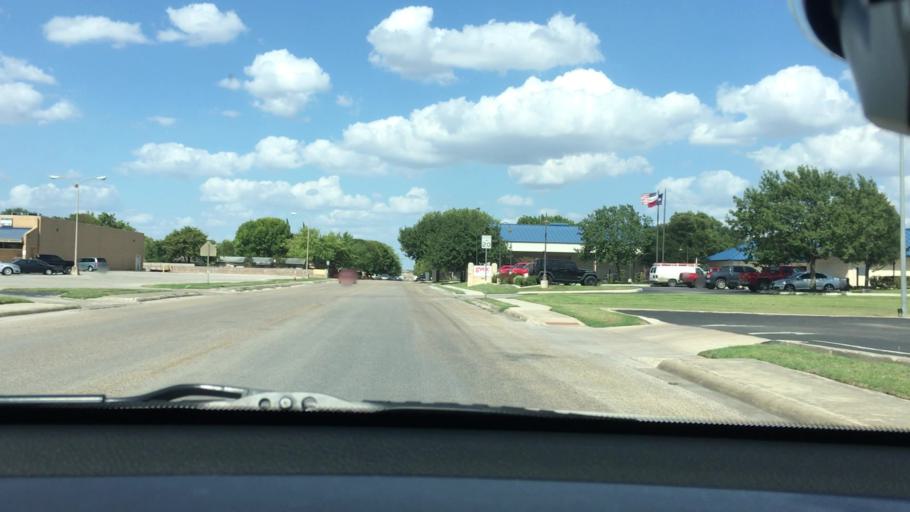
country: US
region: Texas
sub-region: Guadalupe County
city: Schertz
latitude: 29.5578
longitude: -98.2651
